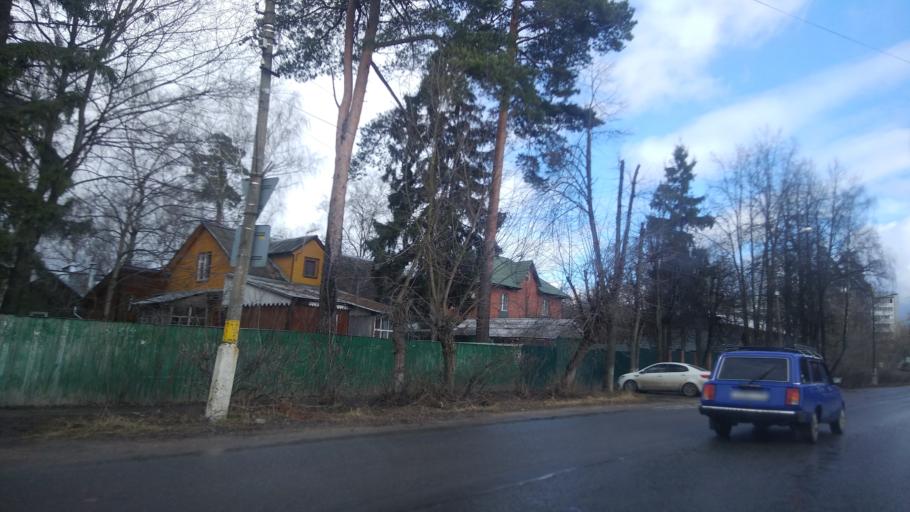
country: RU
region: Moskovskaya
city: Mamontovka
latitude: 56.0084
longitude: 37.8308
